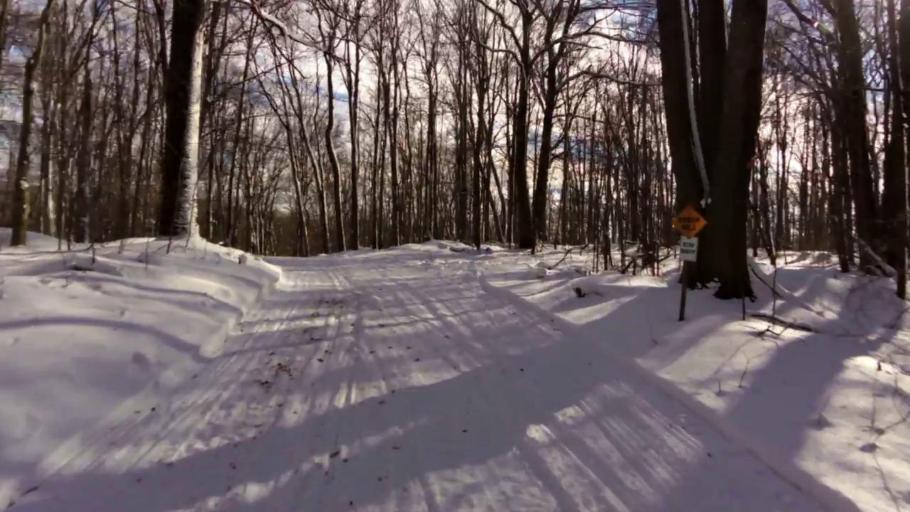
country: US
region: New York
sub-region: Cattaraugus County
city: Salamanca
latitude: 42.0692
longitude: -78.6746
